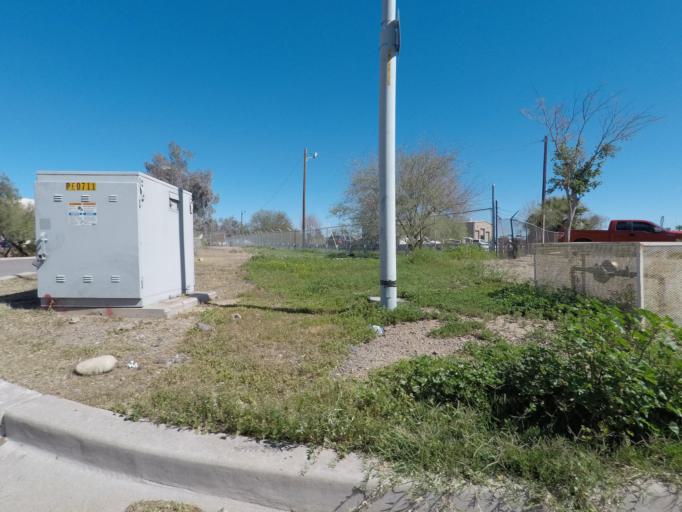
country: US
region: Arizona
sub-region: Maricopa County
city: Tempe Junction
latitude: 33.4146
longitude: -111.9857
